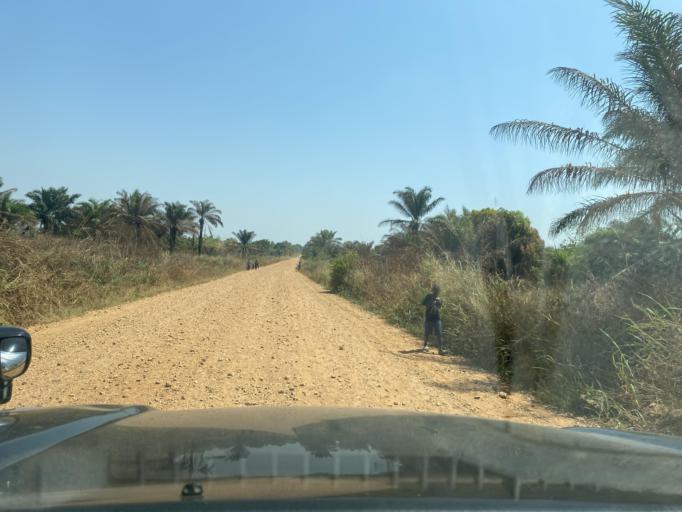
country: CD
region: Kasai-Oriental
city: Mbuji-Mayi
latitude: -6.2588
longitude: 23.7701
